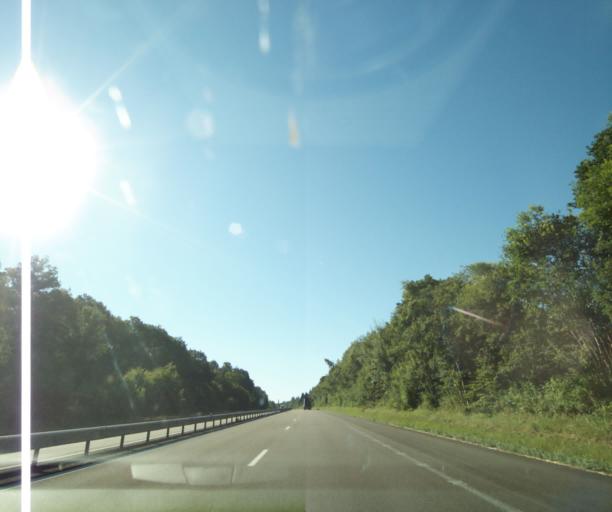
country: FR
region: Champagne-Ardenne
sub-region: Departement de l'Aube
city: Lusigny-sur-Barse
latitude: 48.1834
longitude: 4.2860
